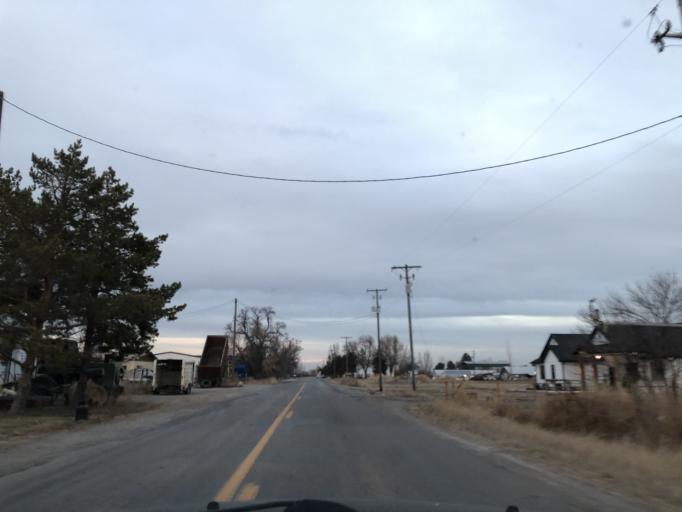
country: US
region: Utah
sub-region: Cache County
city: Benson
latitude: 41.7864
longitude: -111.9118
